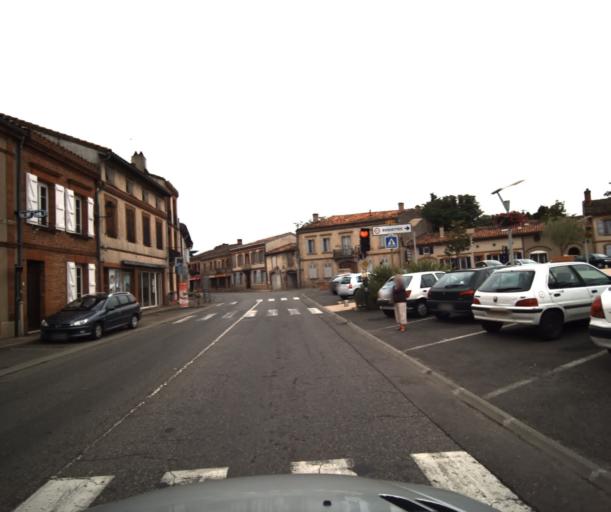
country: FR
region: Midi-Pyrenees
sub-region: Departement de la Haute-Garonne
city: Pinsaguel
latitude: 43.5102
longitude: 1.3887
